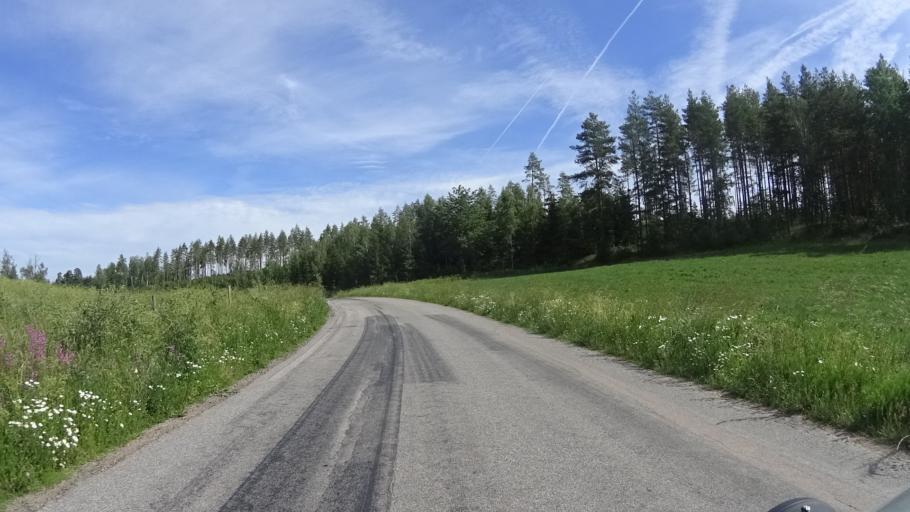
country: SE
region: Kalmar
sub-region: Vasterviks Kommun
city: Overum
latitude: 57.8784
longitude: 16.1765
